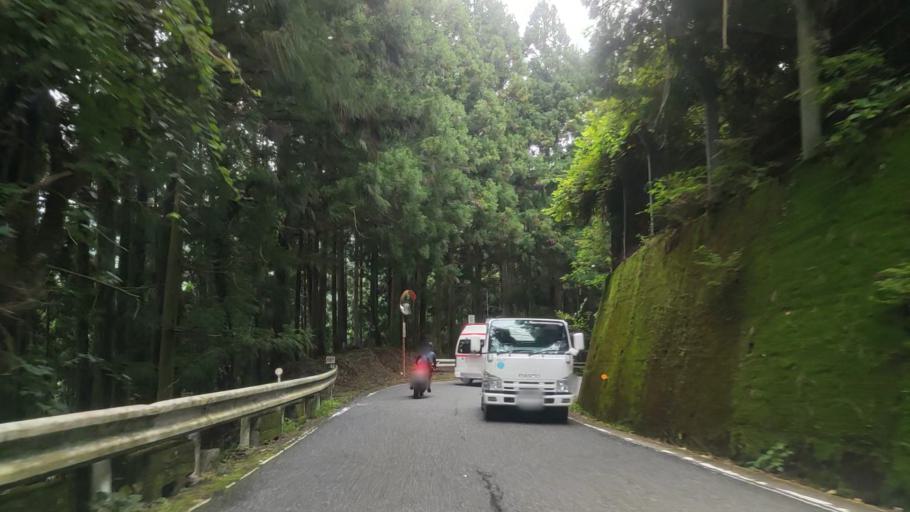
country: JP
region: Wakayama
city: Koya
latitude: 34.2215
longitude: 135.5369
